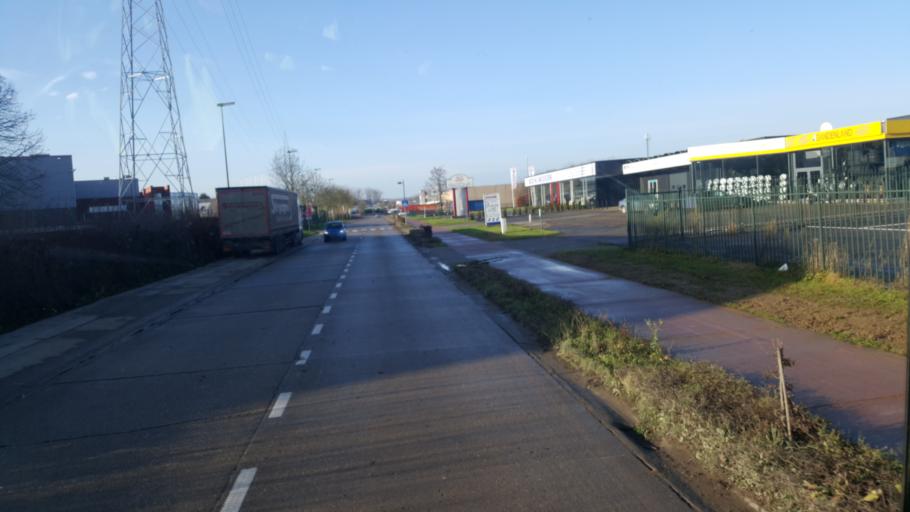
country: BE
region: Flanders
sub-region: Provincie Limburg
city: Maasmechelen
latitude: 50.9485
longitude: 5.7020
